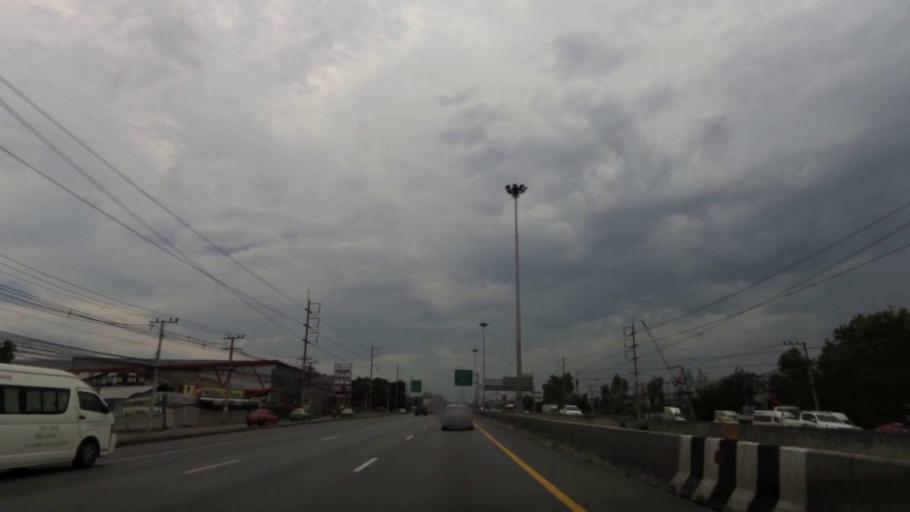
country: TH
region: Pathum Thani
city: Khlong Luang
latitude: 14.0553
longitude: 100.6170
